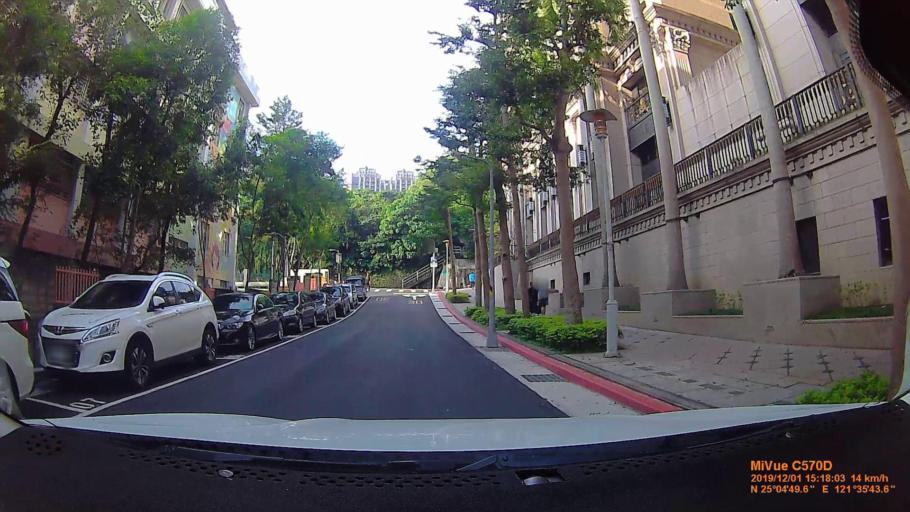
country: TW
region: Taipei
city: Taipei
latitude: 25.0805
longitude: 121.5954
